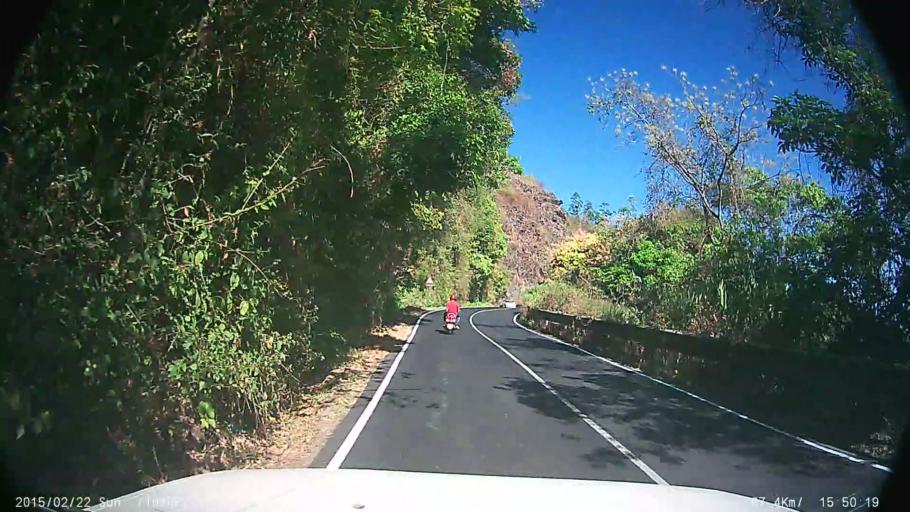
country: IN
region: Kerala
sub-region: Kottayam
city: Erattupetta
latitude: 9.5702
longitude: 77.0022
